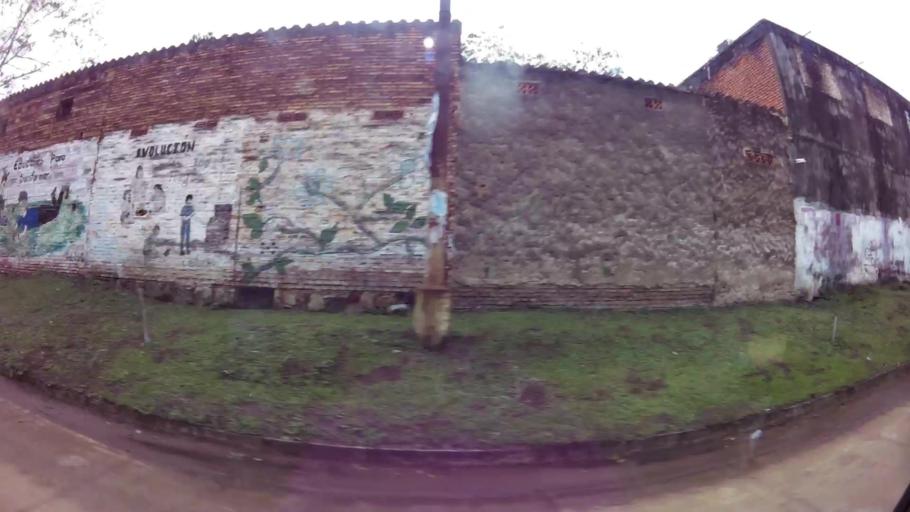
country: PY
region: Central
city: Limpio
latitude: -25.1643
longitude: -57.4761
